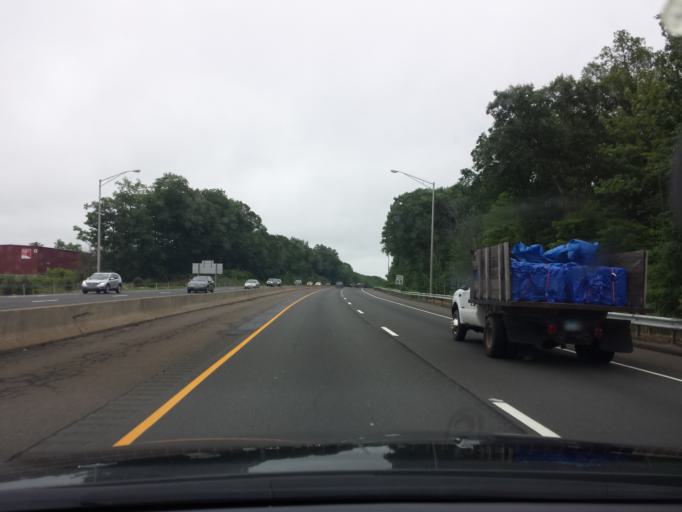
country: US
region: Connecticut
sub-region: New Haven County
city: North Branford
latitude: 41.2967
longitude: -72.7547
